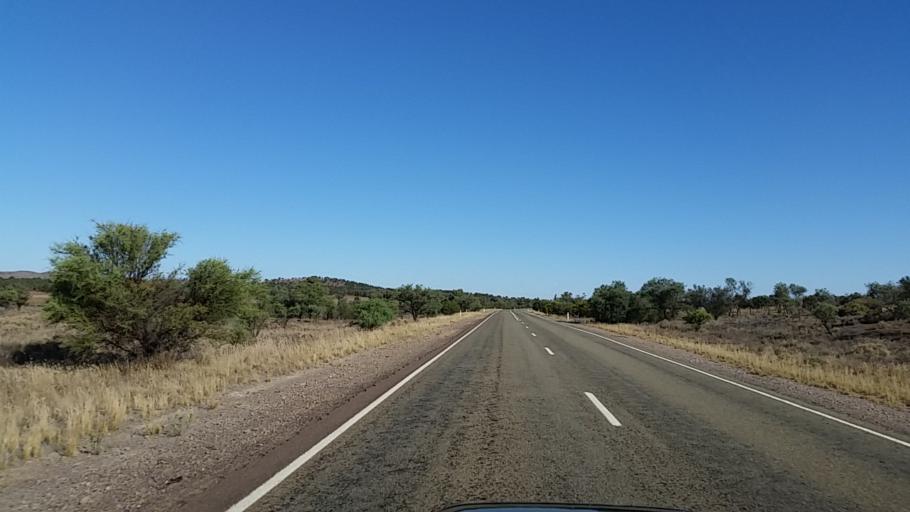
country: AU
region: South Australia
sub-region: Flinders Ranges
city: Quorn
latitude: -32.4969
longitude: 138.5476
